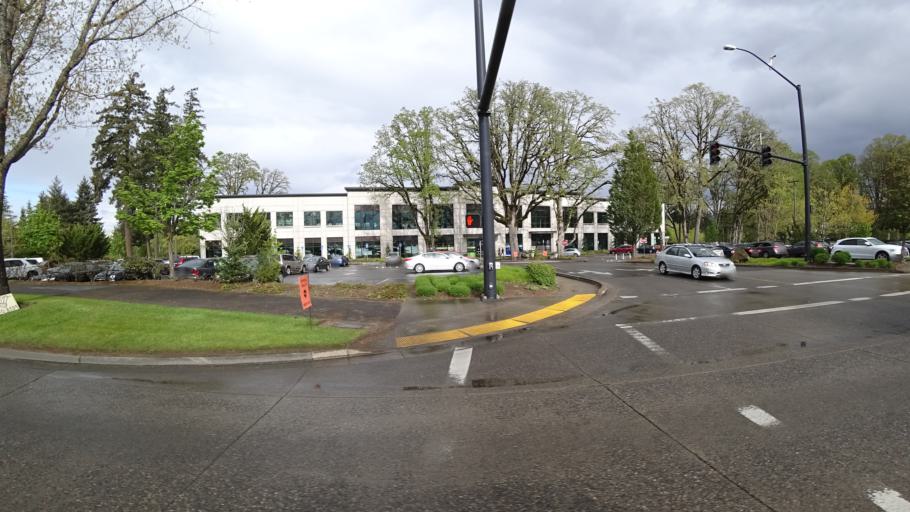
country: US
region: Oregon
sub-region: Washington County
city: Hillsboro
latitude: 45.5428
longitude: -122.9371
